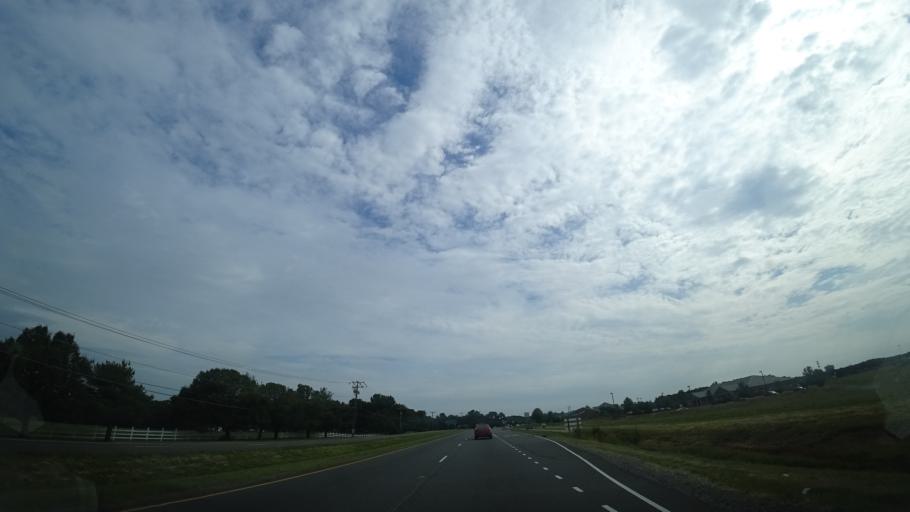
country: US
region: Virginia
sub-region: Spotsylvania County
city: Spotsylvania
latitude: 38.2305
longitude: -77.5617
